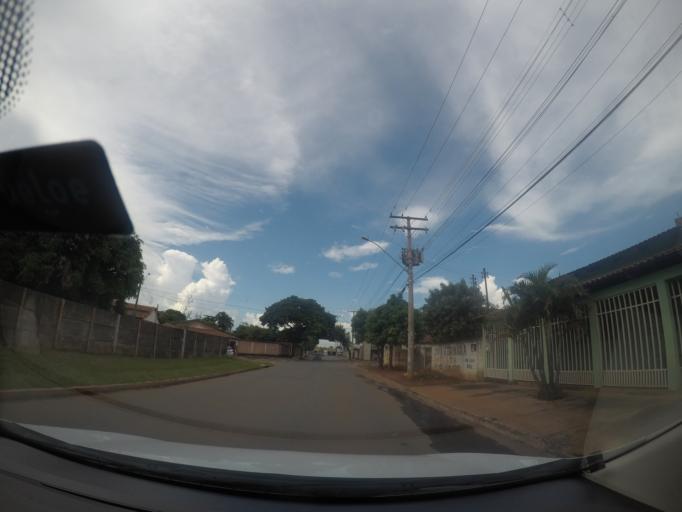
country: BR
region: Goias
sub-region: Goiania
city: Goiania
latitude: -16.7049
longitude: -49.3581
